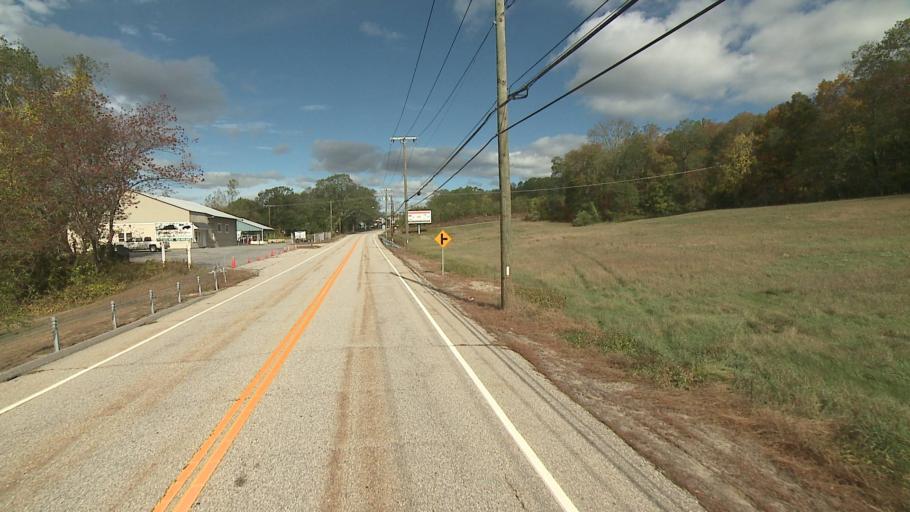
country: US
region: Connecticut
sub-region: Windham County
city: Putnam
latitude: 41.9347
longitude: -71.8946
